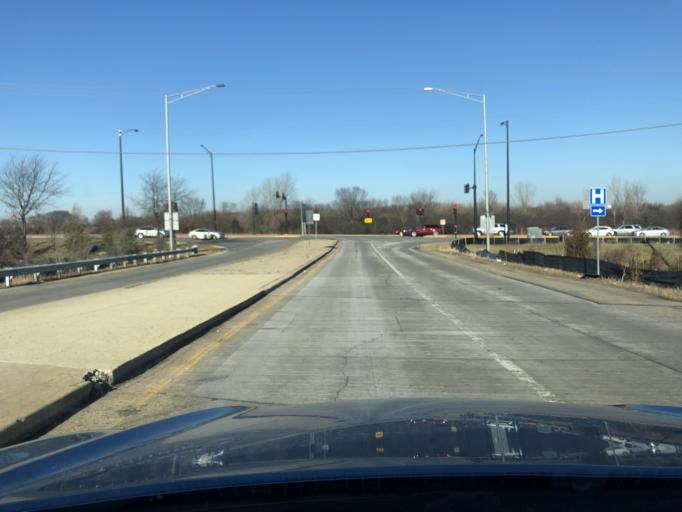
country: US
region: Illinois
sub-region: DuPage County
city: Itasca
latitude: 42.0026
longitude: -88.0237
